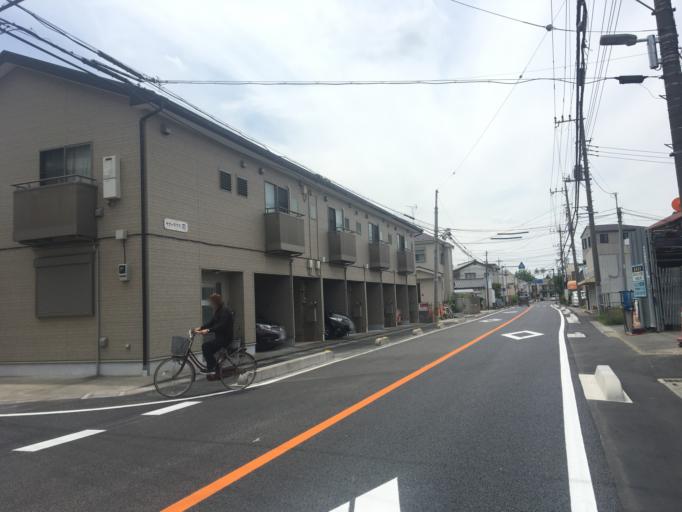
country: JP
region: Saitama
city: Shimotoda
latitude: 35.8290
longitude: 139.6718
